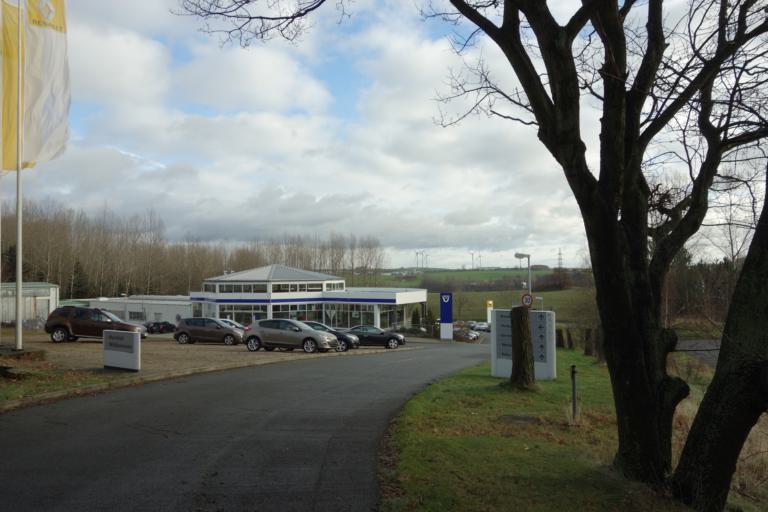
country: DE
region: Saxony
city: Freiberg
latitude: 50.9142
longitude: 13.3672
